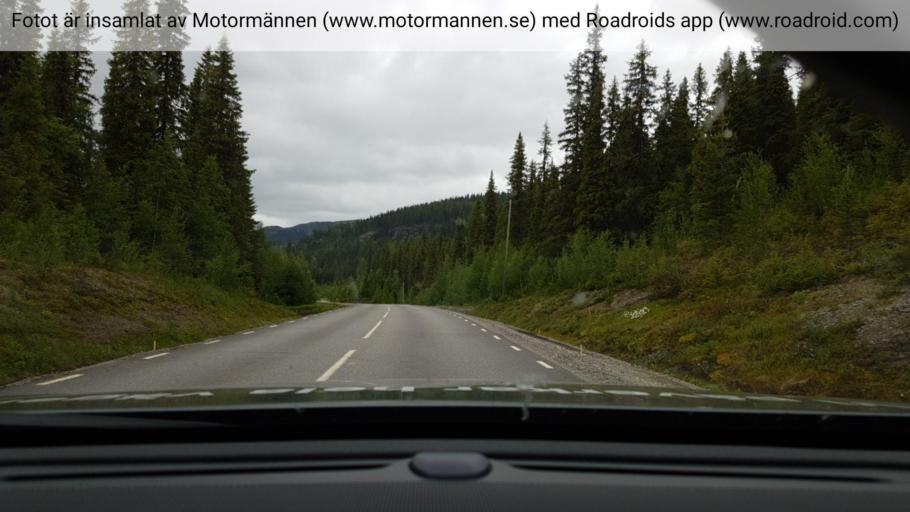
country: SE
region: Vaesterbotten
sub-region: Storumans Kommun
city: Fristad
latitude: 65.8108
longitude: 16.8801
